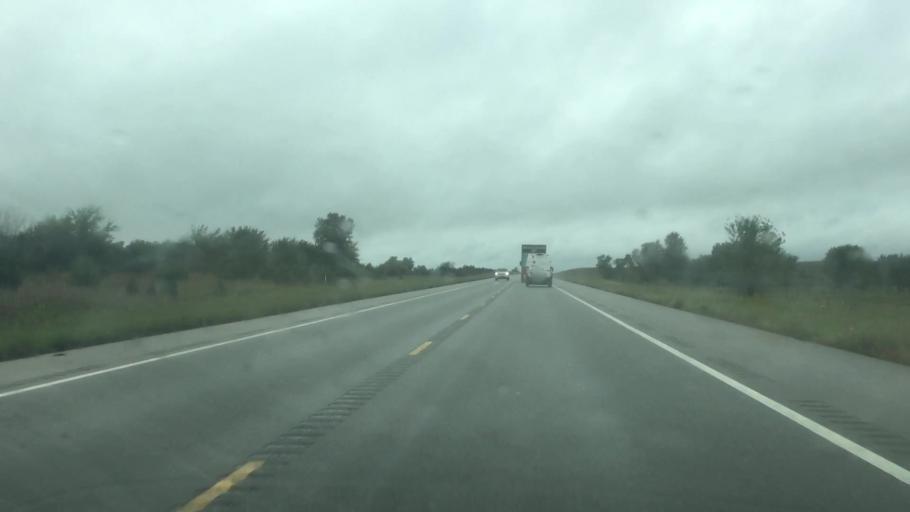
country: US
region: Kansas
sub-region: Allen County
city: Iola
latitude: 38.0954
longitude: -95.3599
